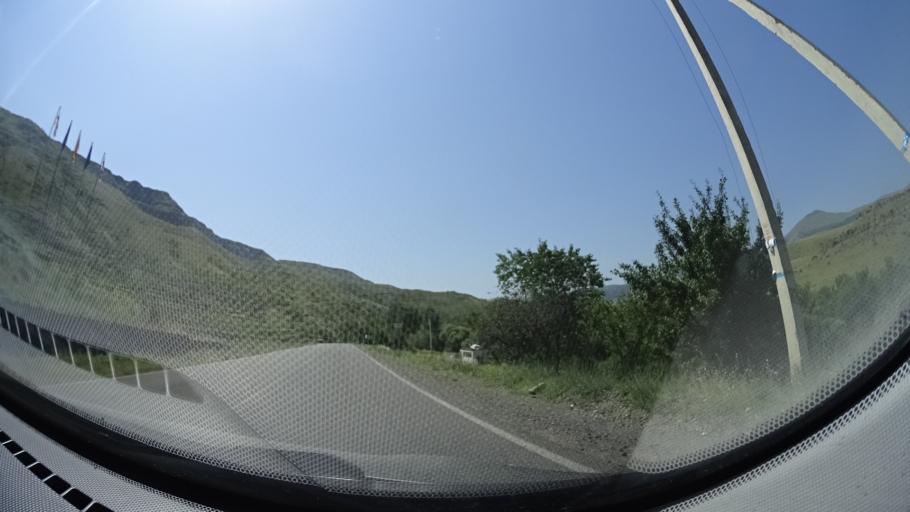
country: GE
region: Samtskhe-Javakheti
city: Aspindza
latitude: 41.5349
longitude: 43.2598
